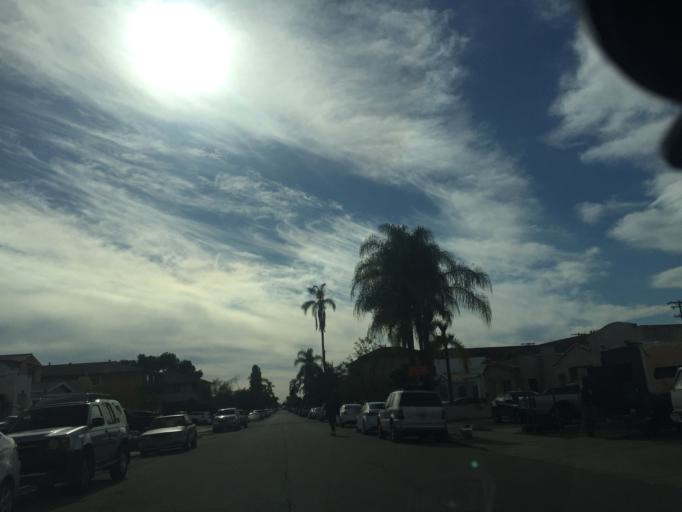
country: US
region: California
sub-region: San Diego County
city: Lemon Grove
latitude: 32.7551
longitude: -117.0944
